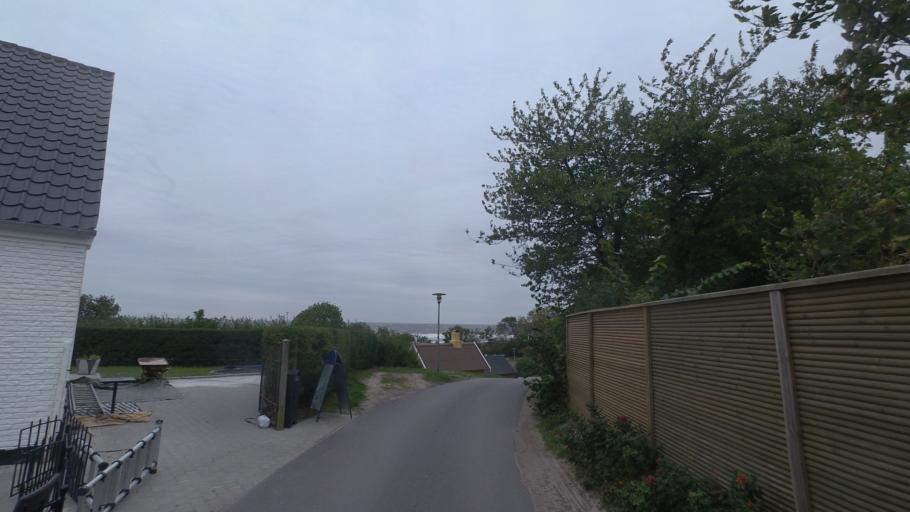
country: DK
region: Capital Region
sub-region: Bornholm Kommune
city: Akirkeby
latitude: 55.0009
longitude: 14.9902
